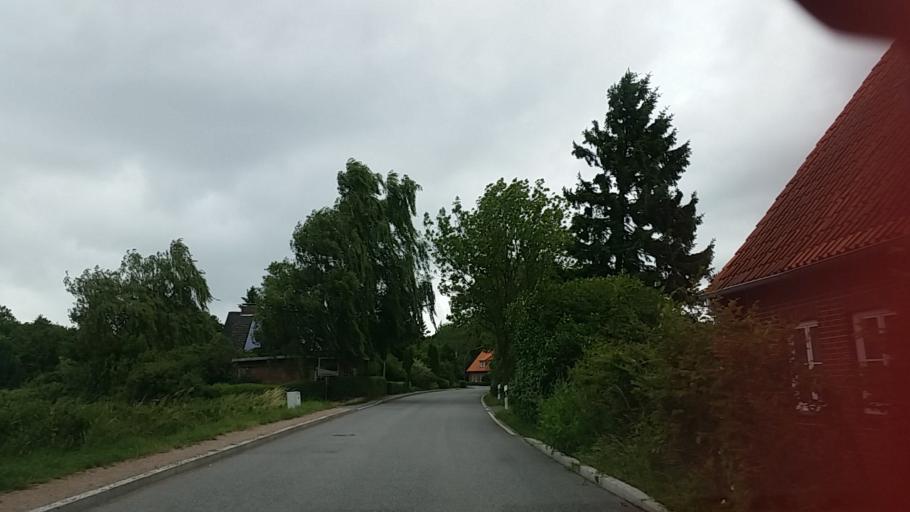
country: DE
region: Schleswig-Holstein
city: Oststeinbek
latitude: 53.5113
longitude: 10.1291
